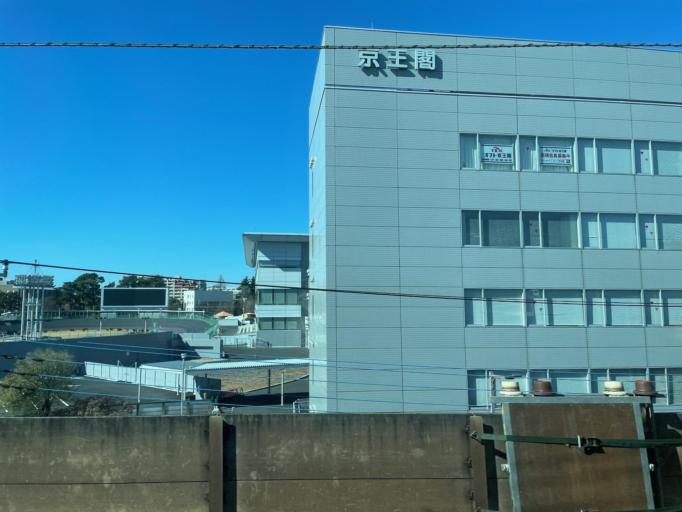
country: JP
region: Tokyo
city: Chofugaoka
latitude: 35.6433
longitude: 139.5356
